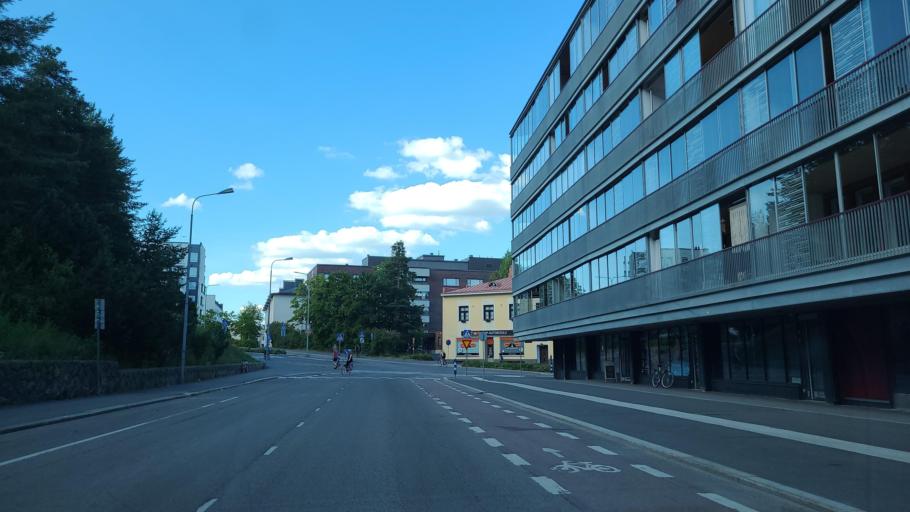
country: FI
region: Central Finland
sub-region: Jyvaeskylae
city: Jyvaeskylae
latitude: 62.2455
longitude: 25.7437
